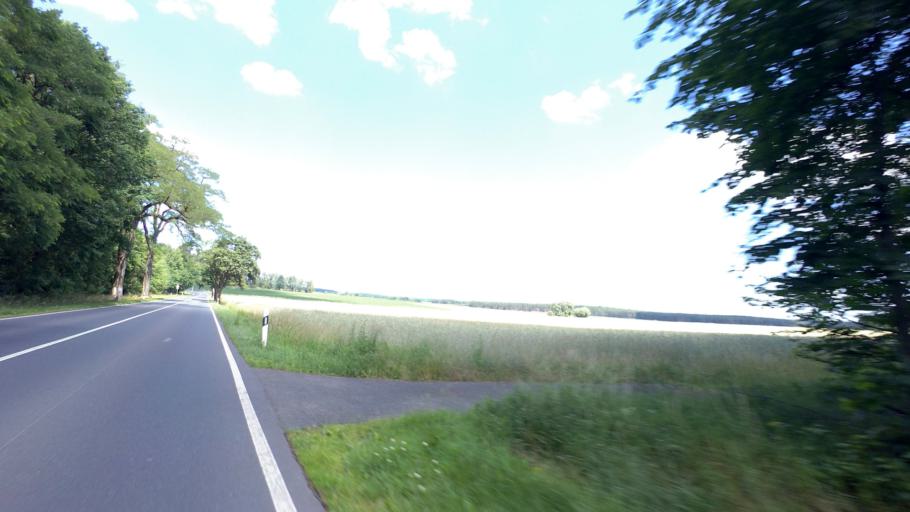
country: DE
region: Brandenburg
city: Kasel-Golzig
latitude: 51.8921
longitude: 13.6849
